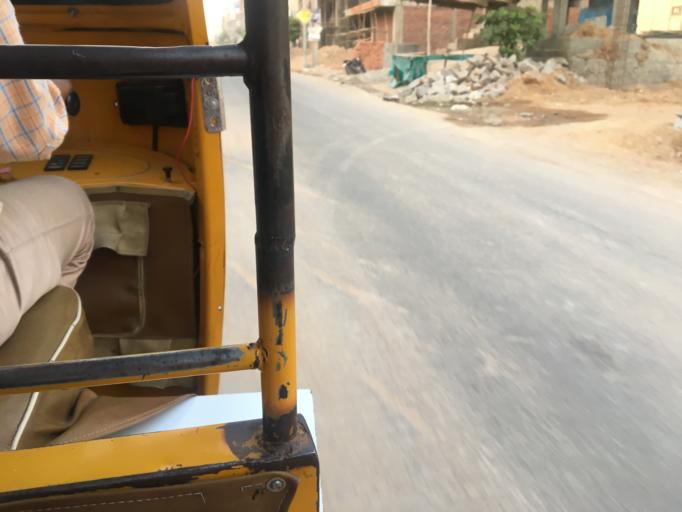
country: IN
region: Telangana
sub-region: Medak
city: Serilingampalle
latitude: 17.4296
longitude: 78.3327
